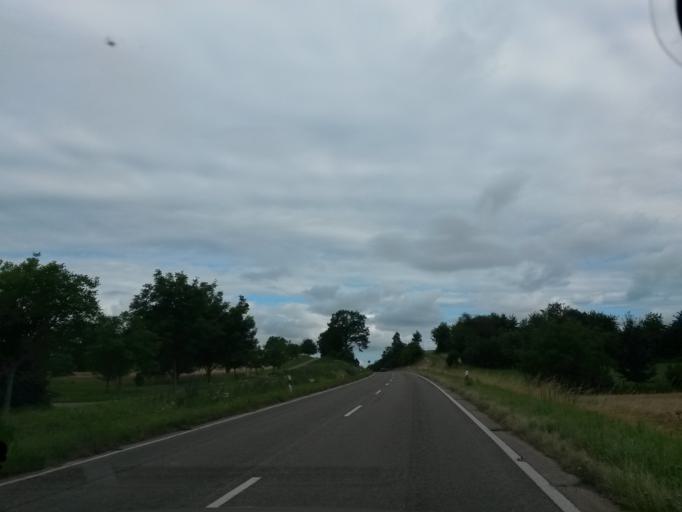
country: DE
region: Baden-Wuerttemberg
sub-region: Karlsruhe Region
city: Konigsbach-Stein
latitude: 48.9133
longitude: 8.5204
